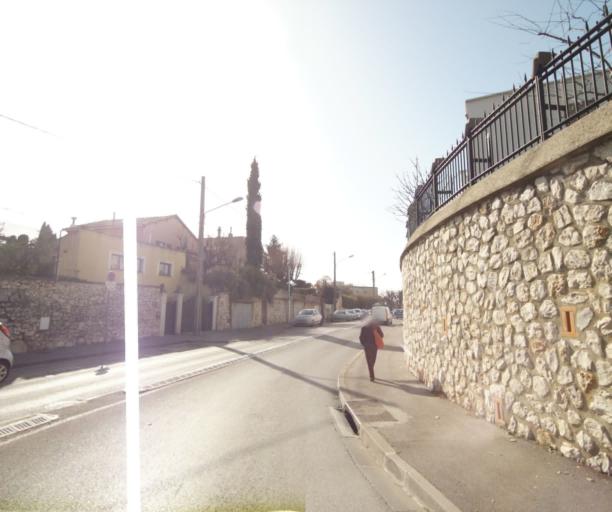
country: FR
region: Provence-Alpes-Cote d'Azur
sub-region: Departement des Bouches-du-Rhone
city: Aix-en-Provence
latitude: 43.5375
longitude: 5.4529
